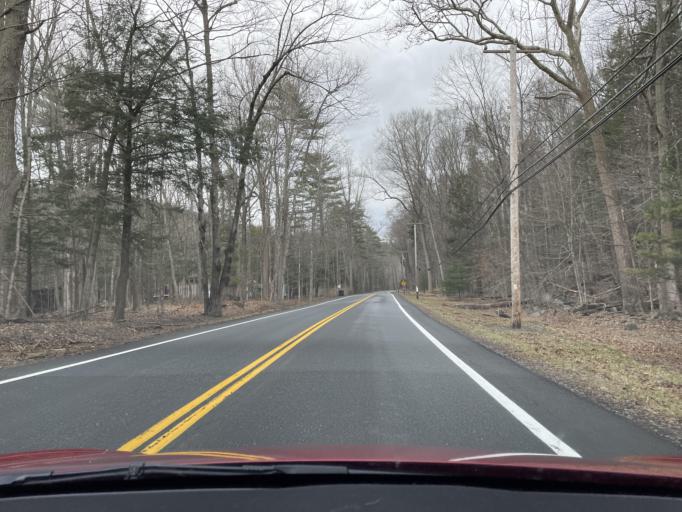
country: US
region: New York
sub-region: Ulster County
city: Woodstock
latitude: 42.0492
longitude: -74.1593
